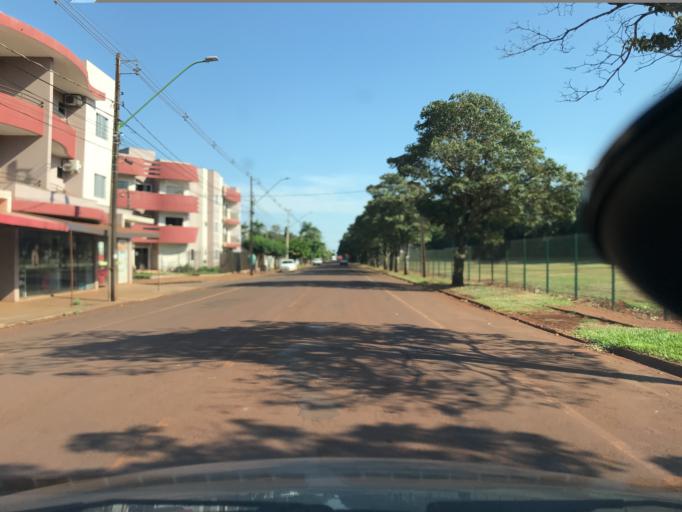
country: BR
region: Parana
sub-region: Palotina
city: Palotina
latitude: -24.2944
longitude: -53.8438
